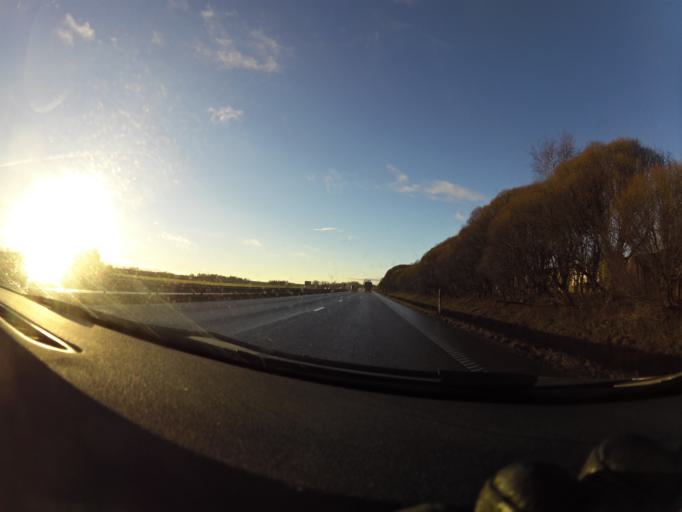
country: SE
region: Gaevleborg
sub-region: Gavle Kommun
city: Valbo
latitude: 60.6609
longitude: 17.0650
